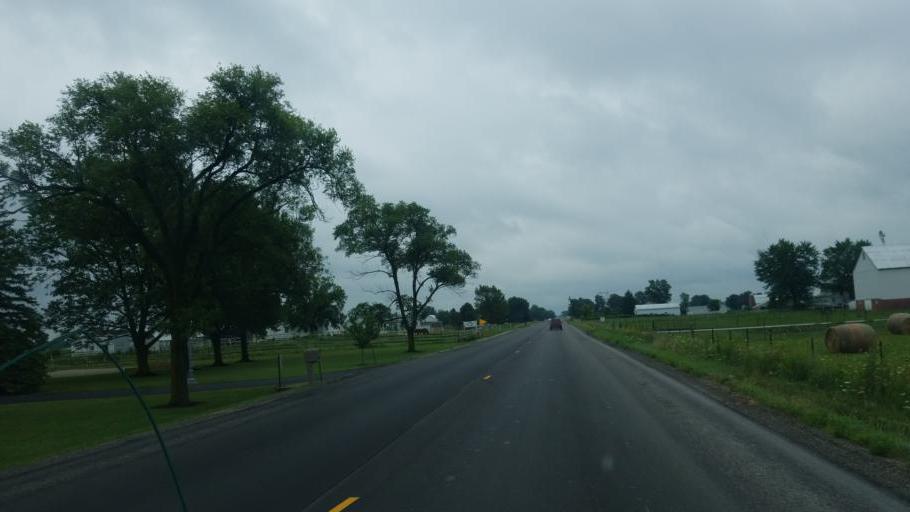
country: US
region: Indiana
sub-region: Adams County
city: Berne
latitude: 40.7114
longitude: -84.9559
